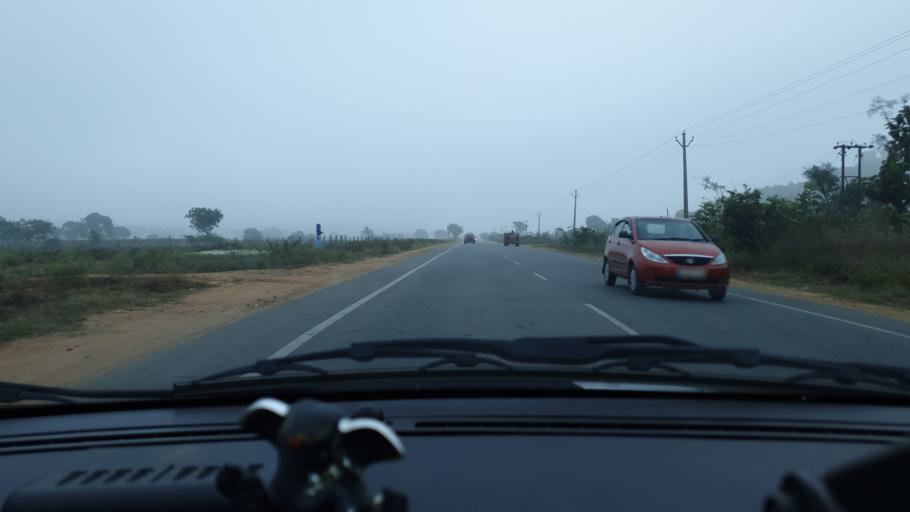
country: IN
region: Telangana
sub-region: Mahbubnagar
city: Farrukhnagar
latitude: 16.9431
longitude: 78.5254
